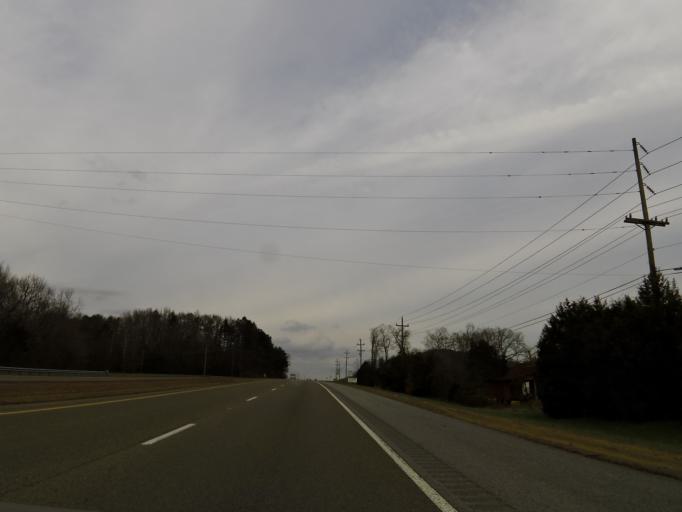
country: US
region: Tennessee
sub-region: Hamilton County
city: Sale Creek
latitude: 35.3617
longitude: -85.1199
